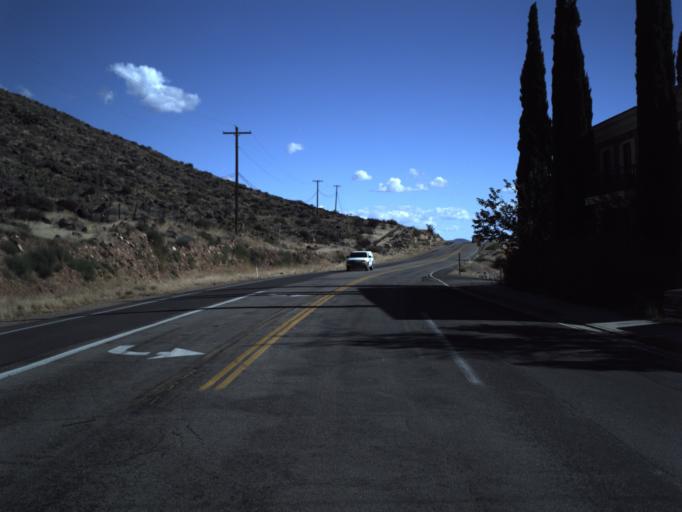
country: US
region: Utah
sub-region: Washington County
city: Toquerville
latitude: 37.2492
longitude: -113.2838
